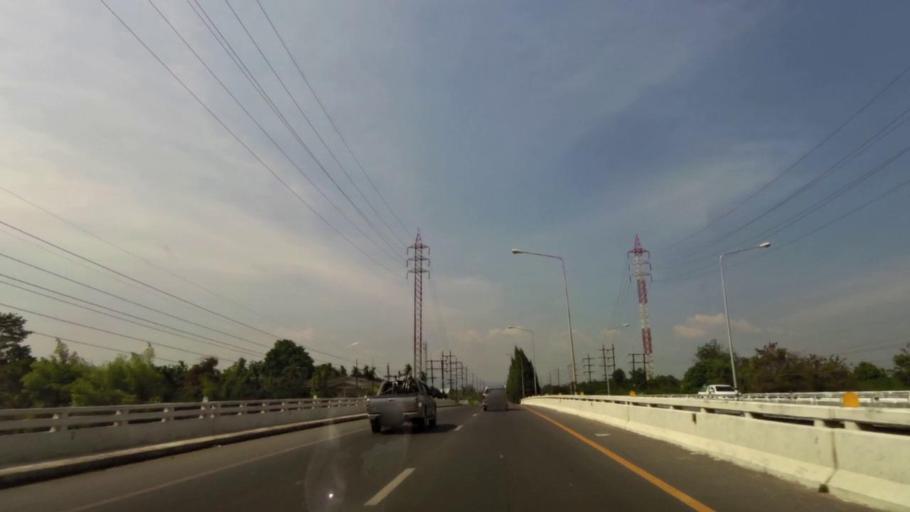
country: TH
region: Chanthaburi
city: Chanthaburi
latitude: 12.6365
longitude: 102.1378
